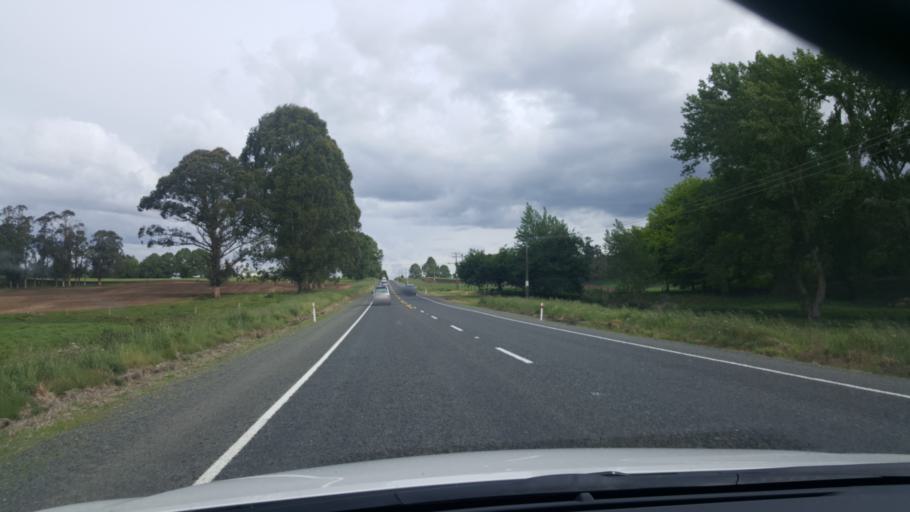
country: NZ
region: Waikato
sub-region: Taupo District
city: Taupo
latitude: -38.4919
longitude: 176.2929
